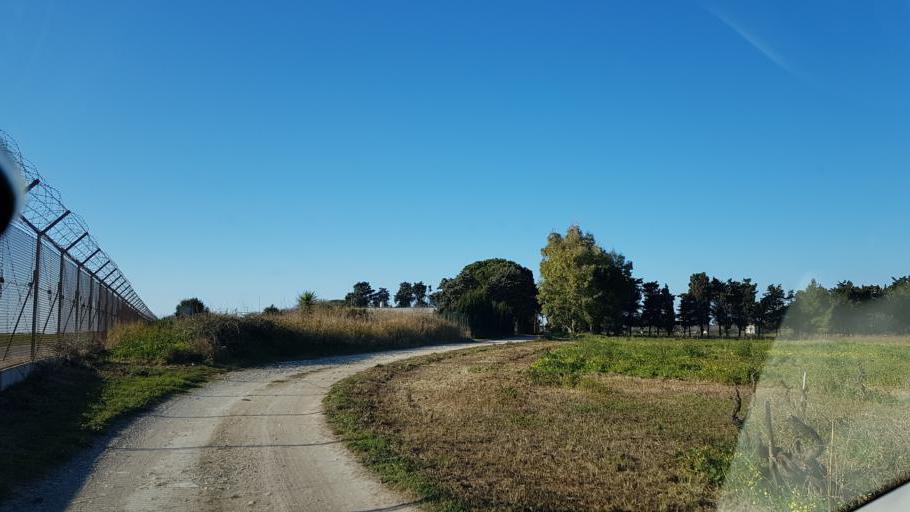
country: IT
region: Apulia
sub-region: Provincia di Brindisi
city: Materdomini
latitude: 40.6693
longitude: 17.9376
